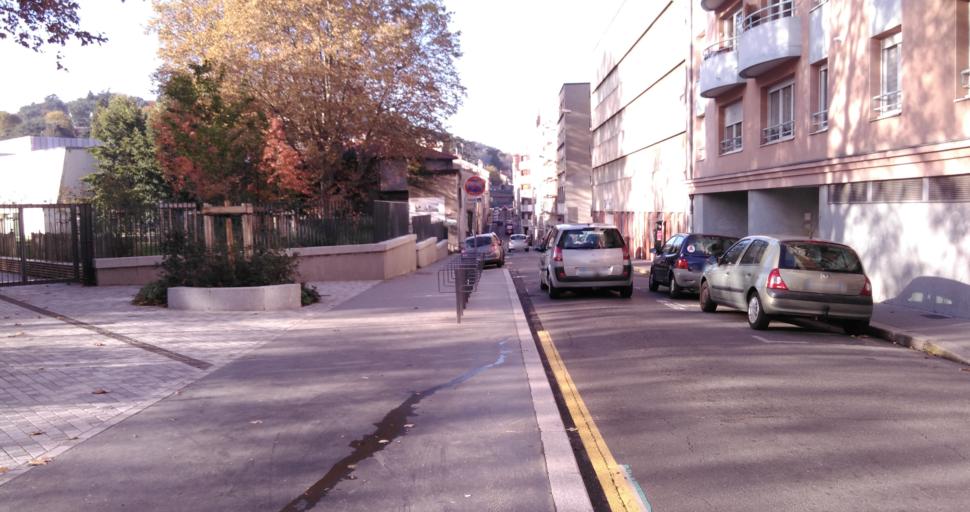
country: FR
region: Rhone-Alpes
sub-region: Departement de la Loire
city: Saint-Etienne
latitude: 45.4429
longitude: 4.3818
